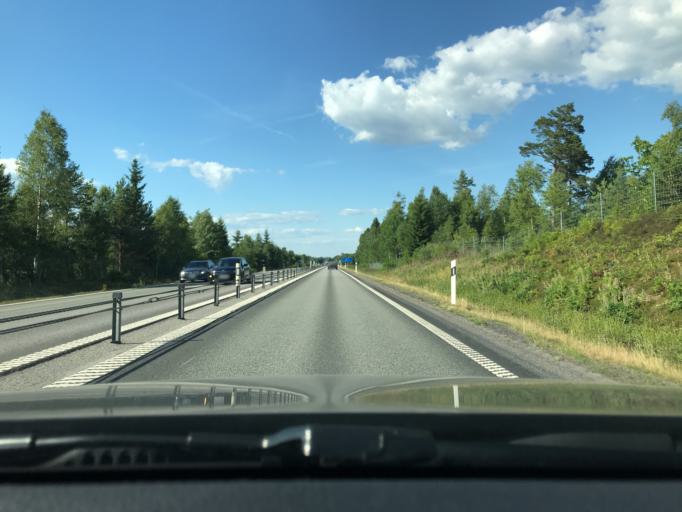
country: SE
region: Kronoberg
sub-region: Almhults Kommun
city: AElmhult
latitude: 56.4929
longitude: 14.1183
